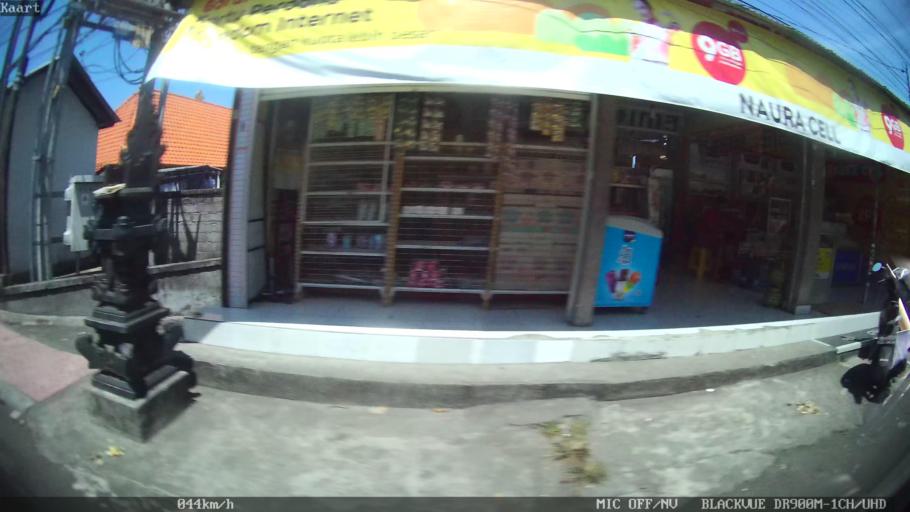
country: ID
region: Bali
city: Klungkung
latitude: -8.5775
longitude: 115.3528
